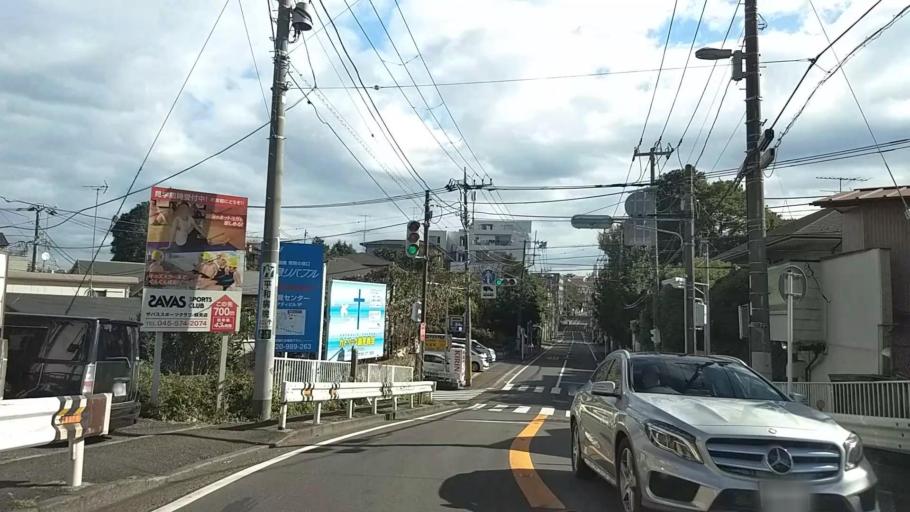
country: JP
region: Kanagawa
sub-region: Kawasaki-shi
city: Kawasaki
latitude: 35.5106
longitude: 139.6666
